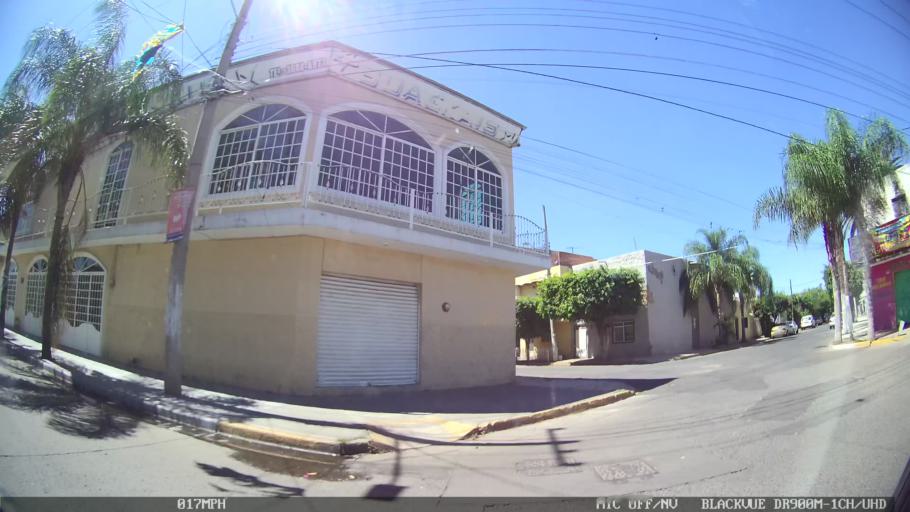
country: MX
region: Jalisco
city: Tlaquepaque
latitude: 20.6660
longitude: -103.2787
